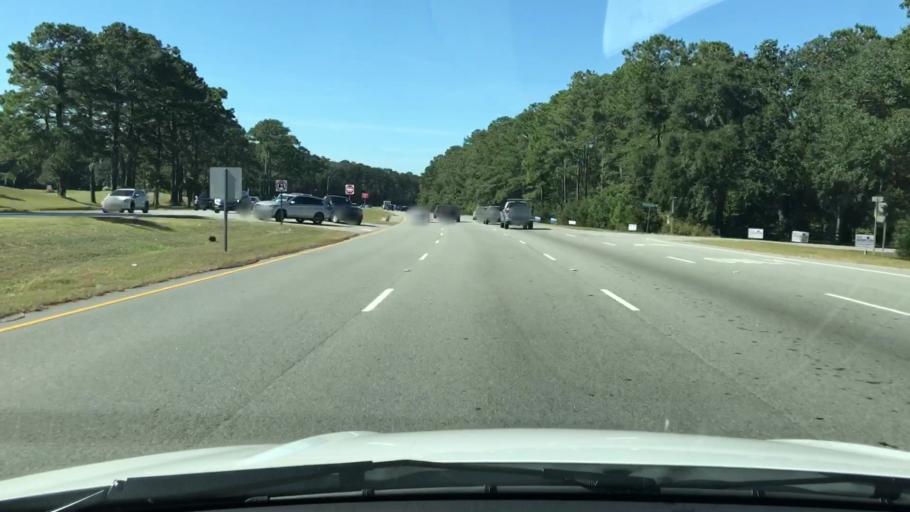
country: US
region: South Carolina
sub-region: Beaufort County
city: Bluffton
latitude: 32.2860
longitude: -80.8872
